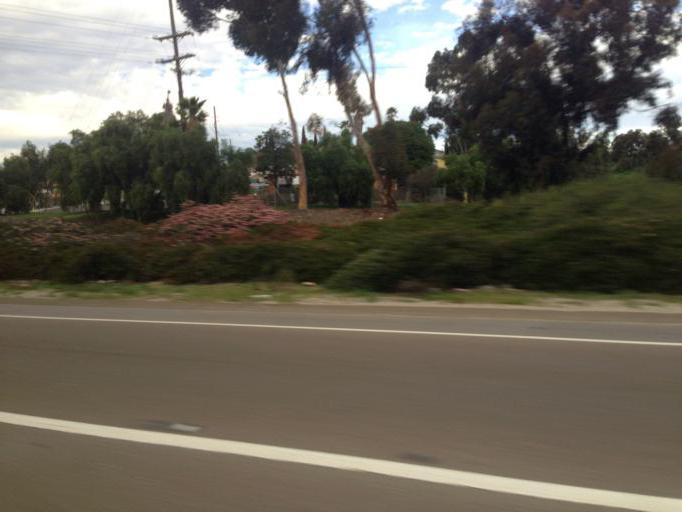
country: US
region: California
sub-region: San Diego County
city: Chula Vista
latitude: 32.6631
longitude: -117.0784
